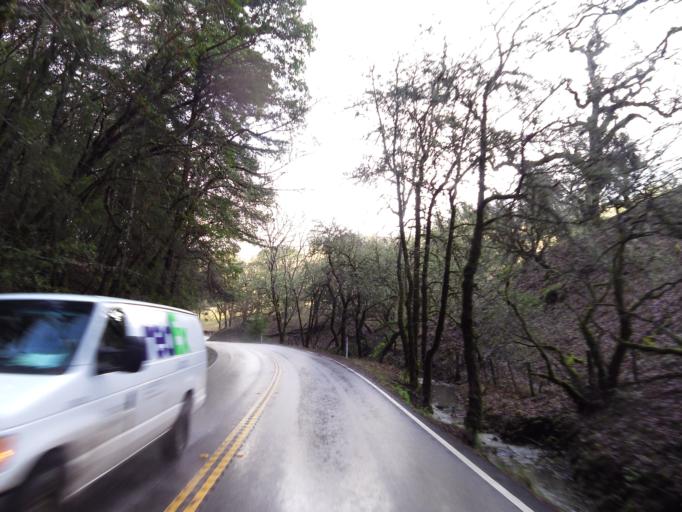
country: US
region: California
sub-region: Sonoma County
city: Cloverdale
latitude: 38.8862
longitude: -123.1221
